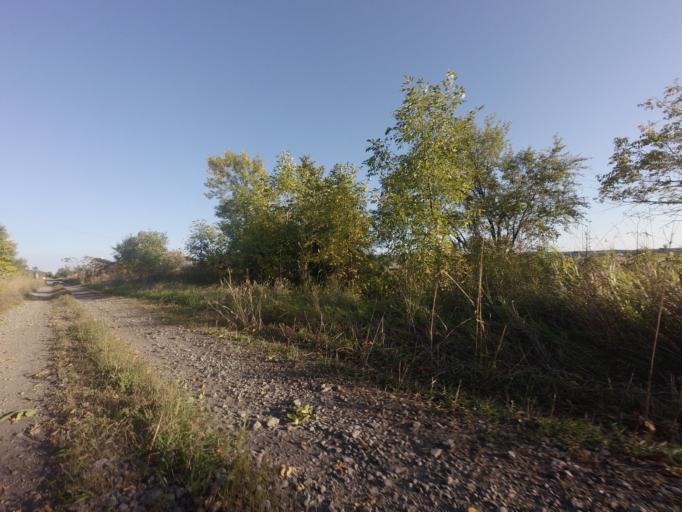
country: CA
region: Quebec
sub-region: Monteregie
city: Rigaud
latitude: 45.4847
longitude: -74.3505
